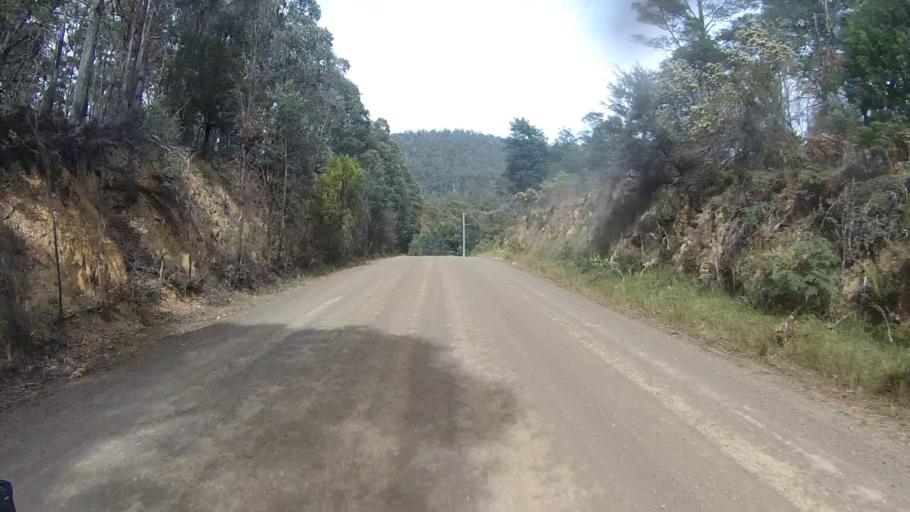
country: AU
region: Tasmania
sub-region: Sorell
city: Sorell
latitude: -42.6893
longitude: 147.8679
